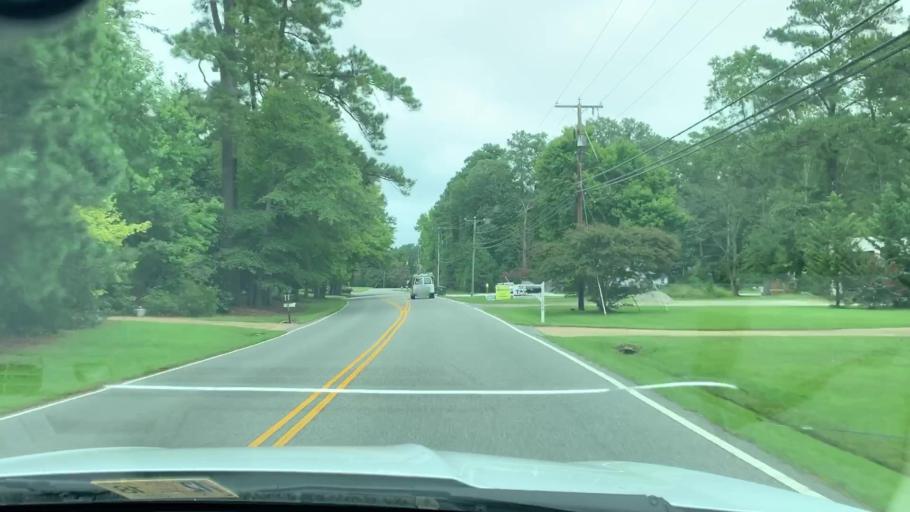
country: US
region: Virginia
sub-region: Gloucester County
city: Gloucester Point
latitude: 37.1914
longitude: -76.4351
